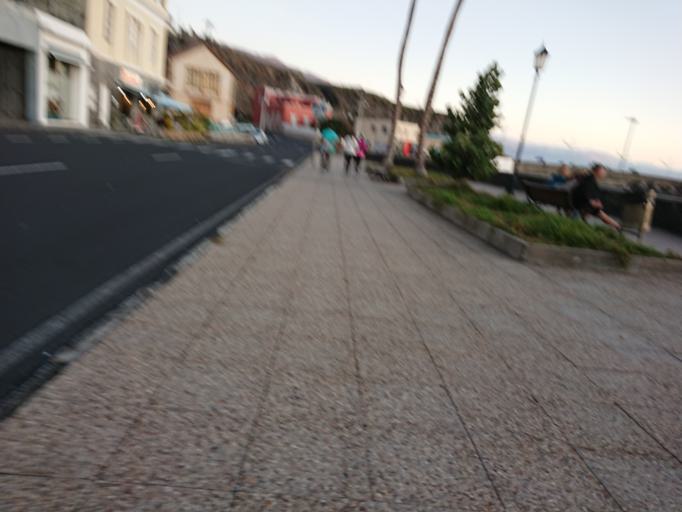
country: ES
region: Canary Islands
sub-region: Provincia de Santa Cruz de Tenerife
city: Tazacorte
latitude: 28.6483
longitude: -17.9444
